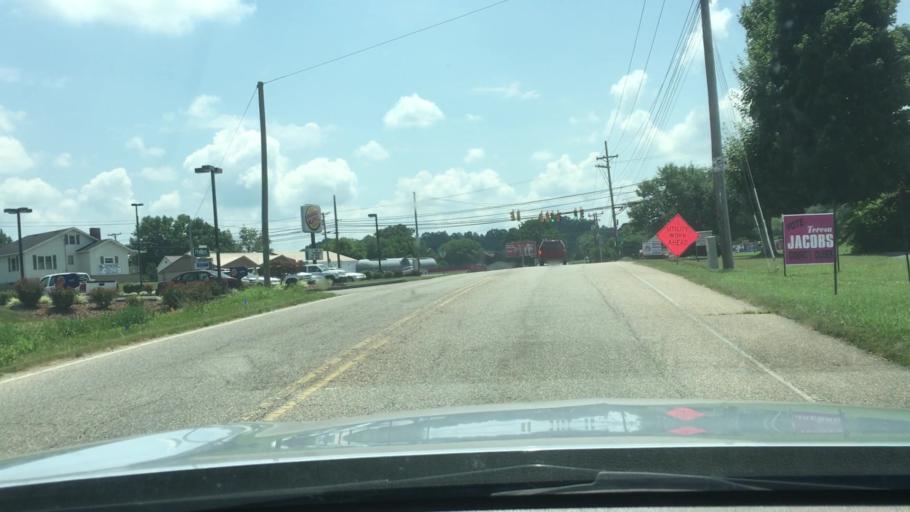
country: US
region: Tennessee
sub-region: Sullivan County
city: Blountville
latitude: 36.5351
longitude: -82.3206
